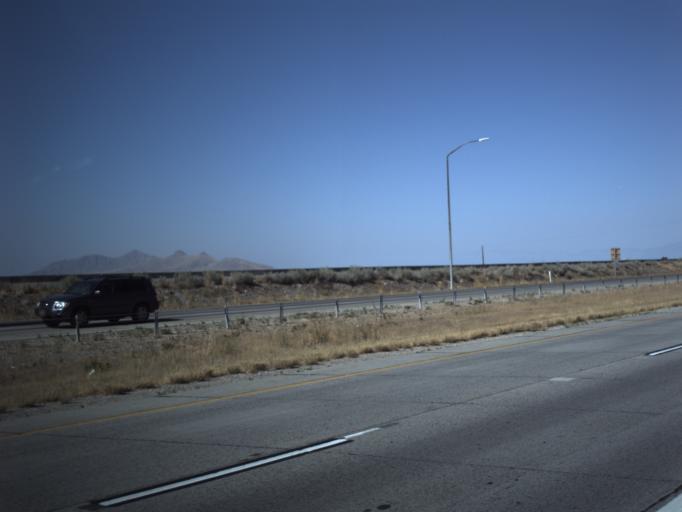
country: US
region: Utah
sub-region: Salt Lake County
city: Magna
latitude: 40.7493
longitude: -112.1780
